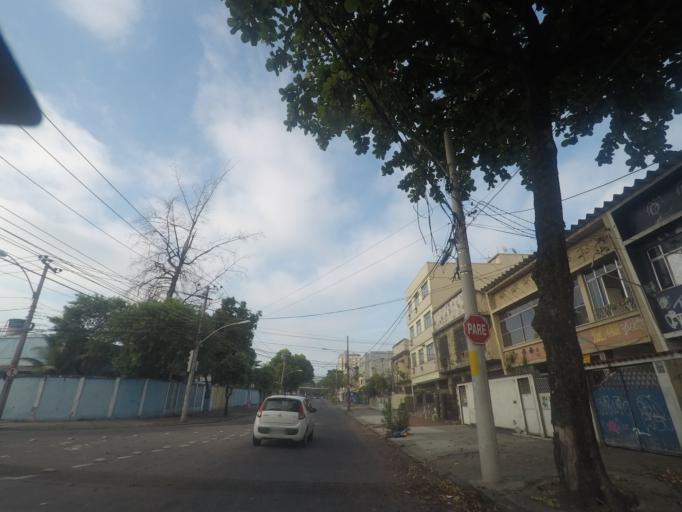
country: BR
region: Rio de Janeiro
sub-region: Duque De Caxias
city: Duque de Caxias
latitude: -22.8394
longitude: -43.2661
